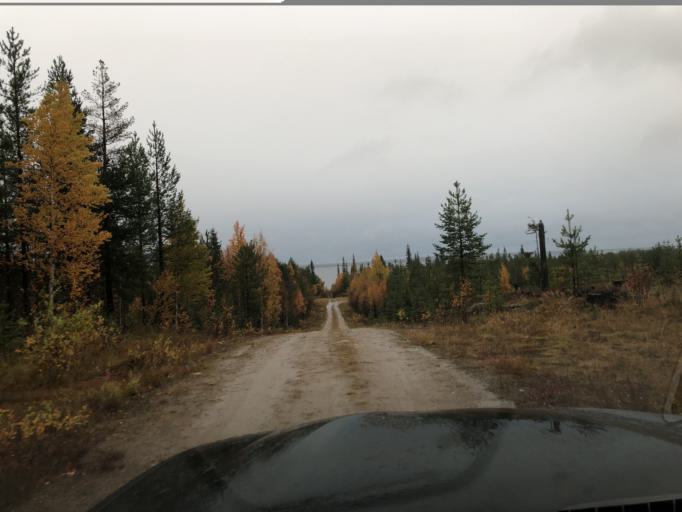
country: FI
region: Lapland
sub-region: Itae-Lappi
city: Posio
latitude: 66.1016
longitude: 28.5433
